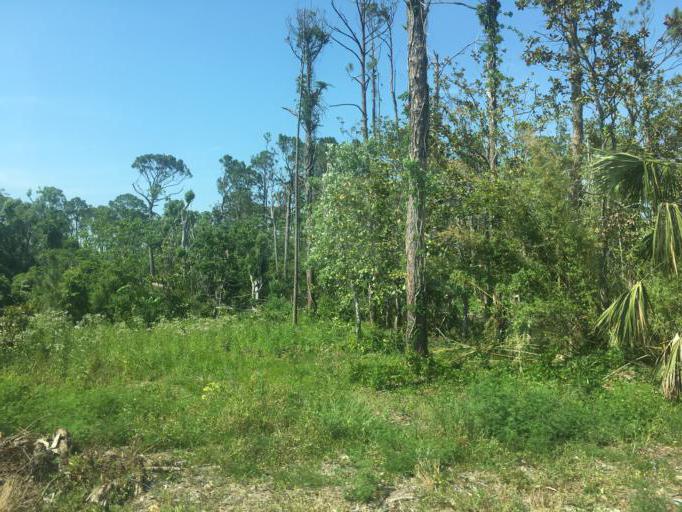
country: US
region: Florida
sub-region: Bay County
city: Upper Grand Lagoon
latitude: 30.1581
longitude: -85.7262
